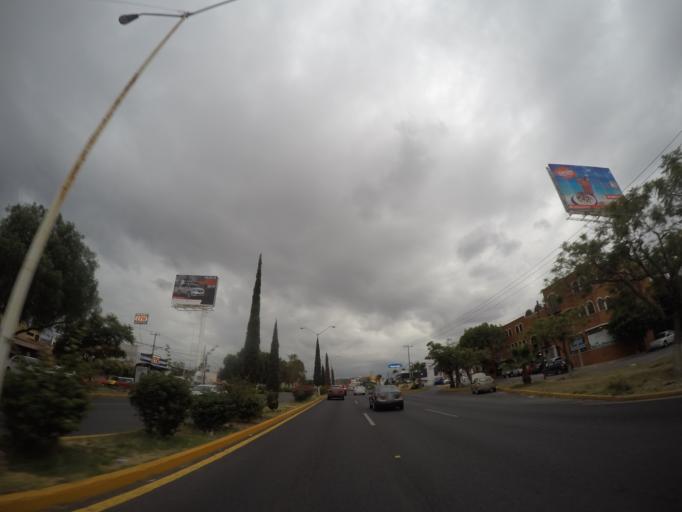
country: MX
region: San Luis Potosi
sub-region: San Luis Potosi
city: San Luis Potosi
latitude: 22.1365
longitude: -101.0268
